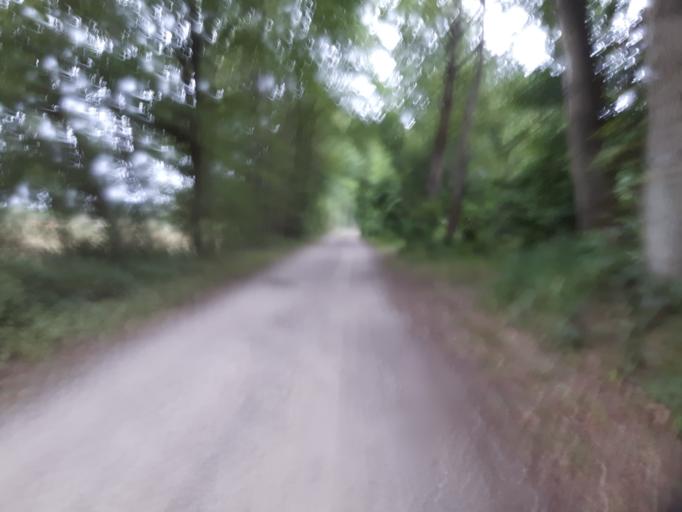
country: DE
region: Lower Saxony
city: Winsen
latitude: 53.3156
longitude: 10.1967
